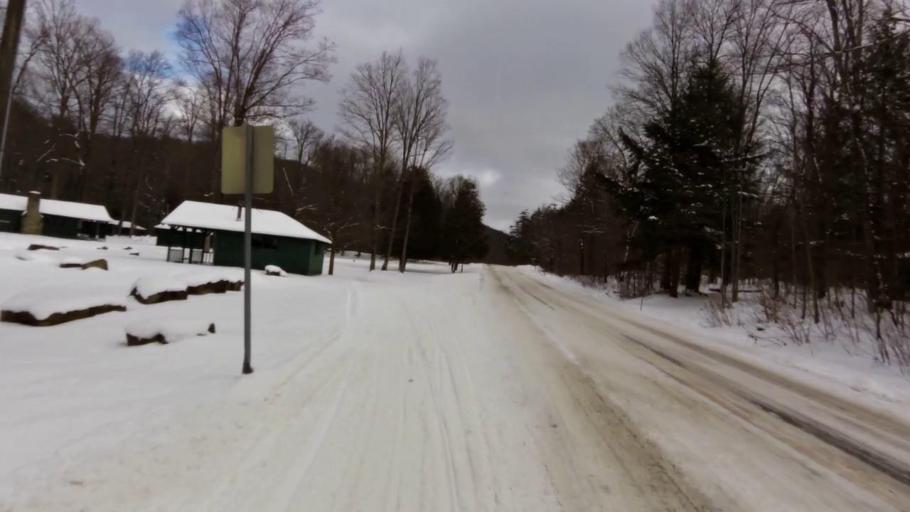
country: US
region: New York
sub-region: Cattaraugus County
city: Salamanca
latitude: 42.0115
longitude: -78.8102
